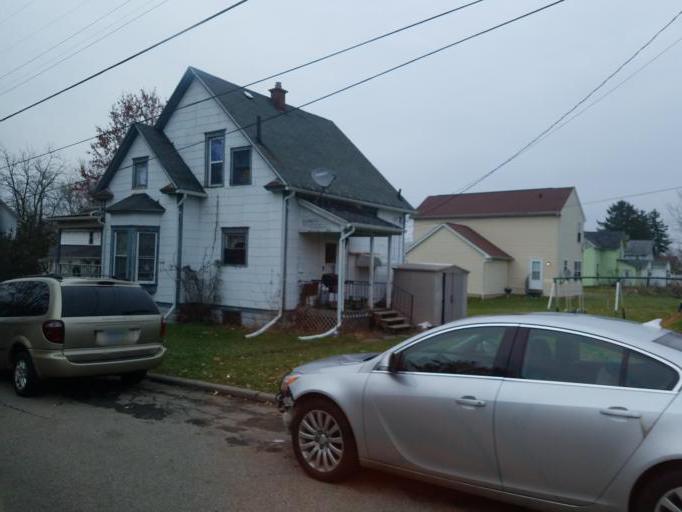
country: US
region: Ohio
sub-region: Richland County
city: Mansfield
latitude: 40.7522
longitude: -82.5078
